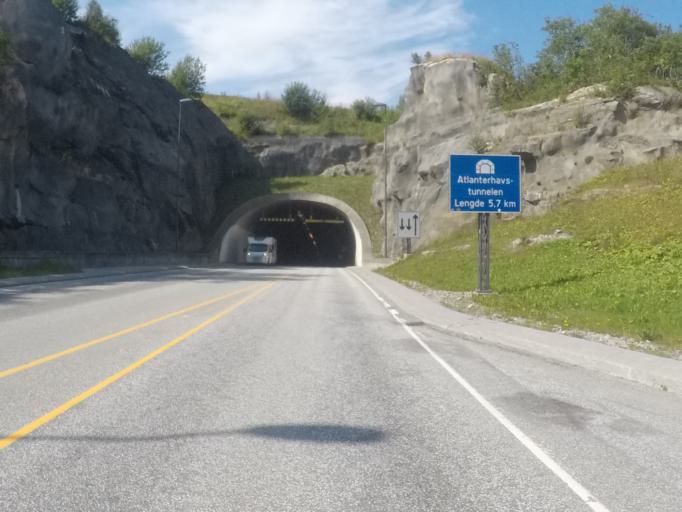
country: NO
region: More og Romsdal
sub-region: Kristiansund
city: Kristiansund
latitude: 63.1255
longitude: 7.7259
